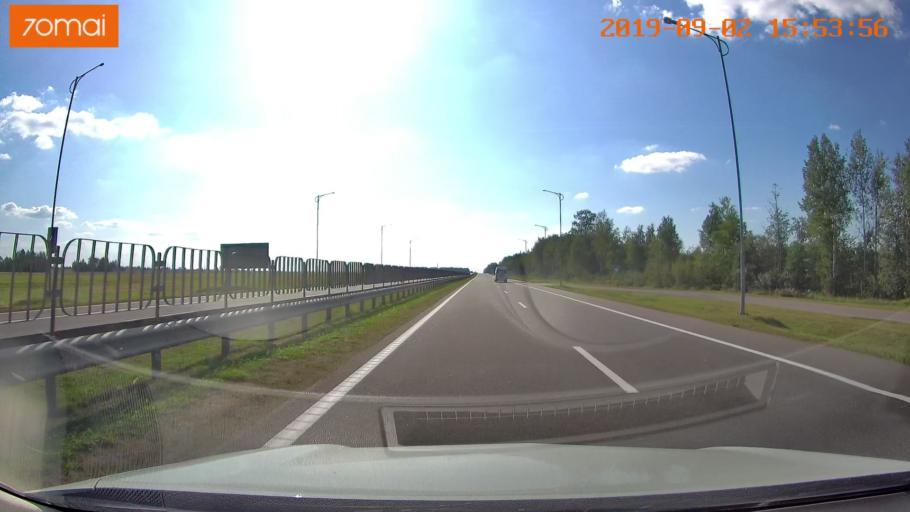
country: BY
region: Minsk
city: Byerazino
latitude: 53.8567
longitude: 29.1397
